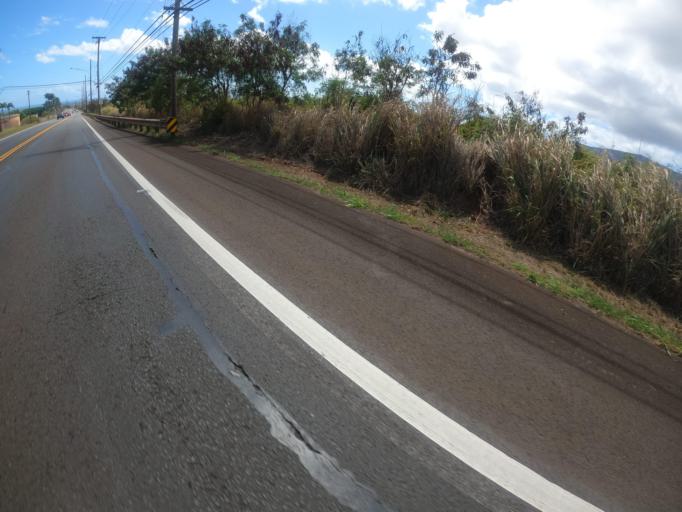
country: US
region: Hawaii
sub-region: Honolulu County
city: Village Park
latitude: 21.4002
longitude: -158.0396
